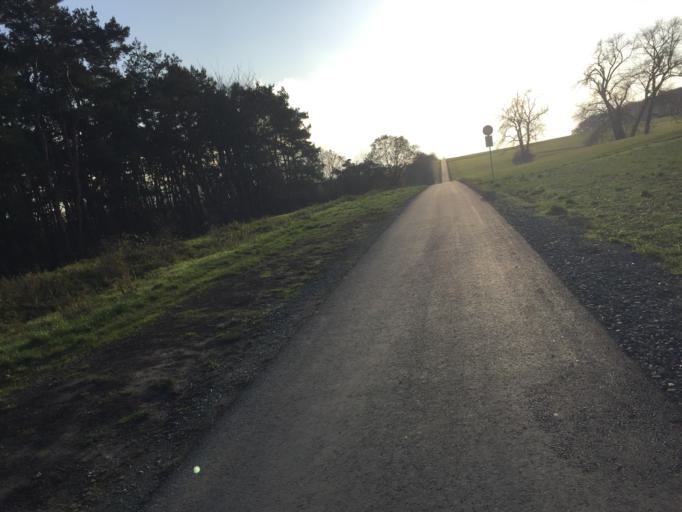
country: DE
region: Hesse
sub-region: Regierungsbezirk Giessen
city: Langgons
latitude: 50.5178
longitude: 8.7135
